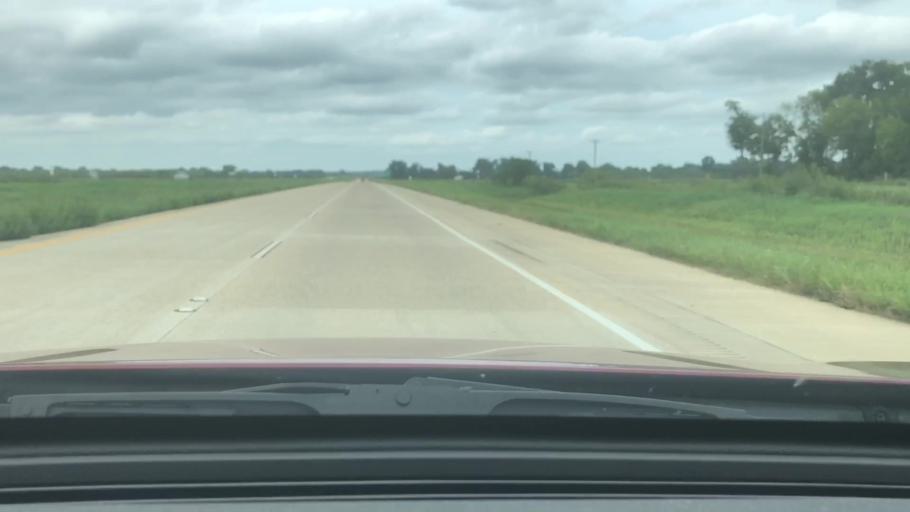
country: US
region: Louisiana
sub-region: Caddo Parish
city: Oil City
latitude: 32.7520
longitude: -93.8822
